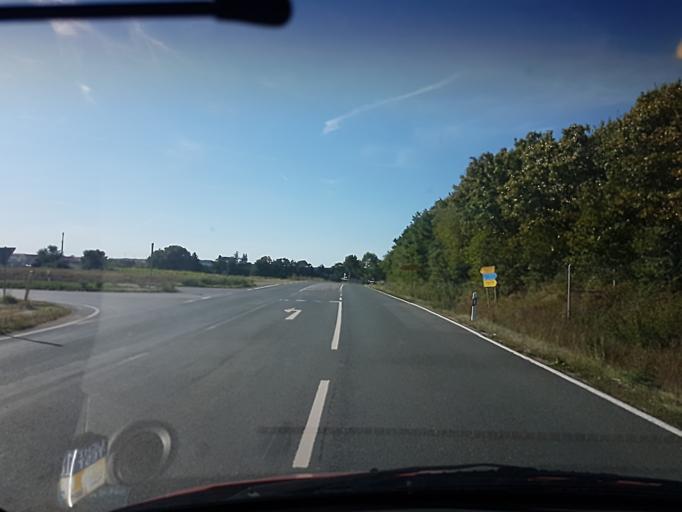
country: DE
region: Bavaria
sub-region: Regierungsbezirk Mittelfranken
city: Adelsdorf
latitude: 49.7073
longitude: 10.9077
